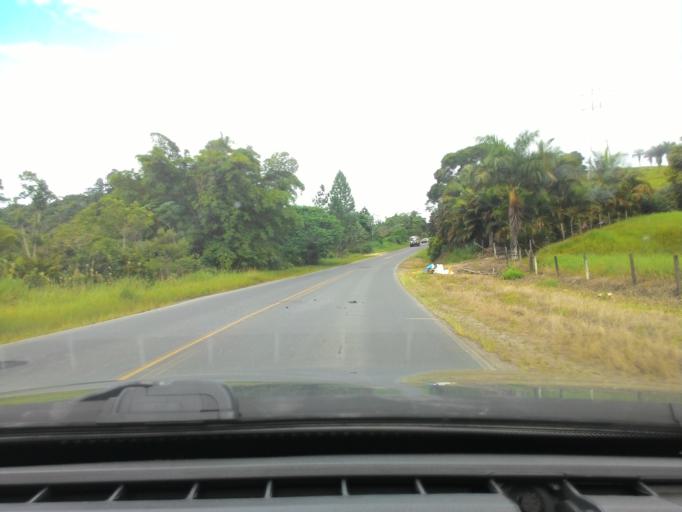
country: BR
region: Sao Paulo
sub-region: Pariquera-Acu
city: Pariquera Acu
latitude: -24.7331
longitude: -47.8384
